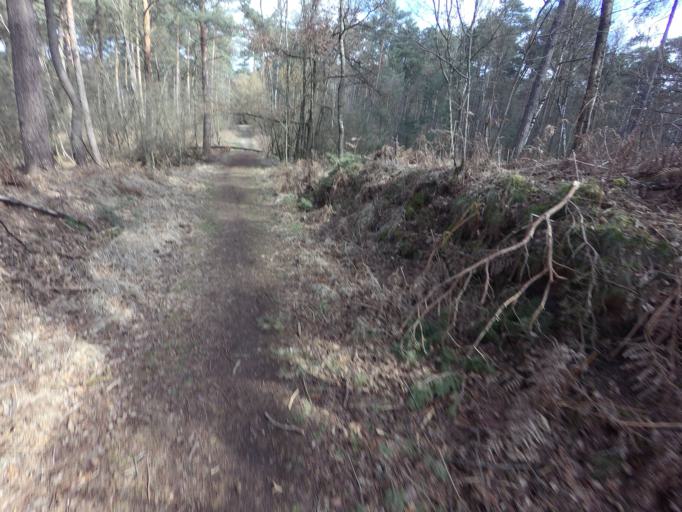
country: NL
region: Limburg
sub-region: Gemeente Roerdalen
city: Herkenbosch
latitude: 51.1717
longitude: 6.0917
